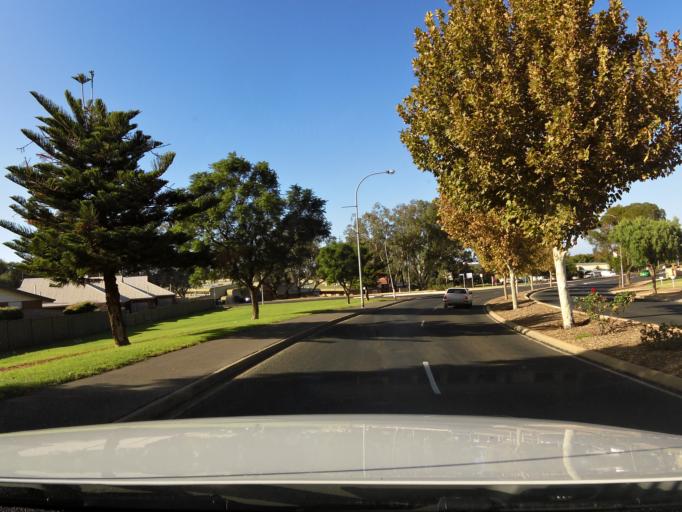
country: AU
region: South Australia
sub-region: Berri and Barmera
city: Berri
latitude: -34.2758
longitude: 140.6101
